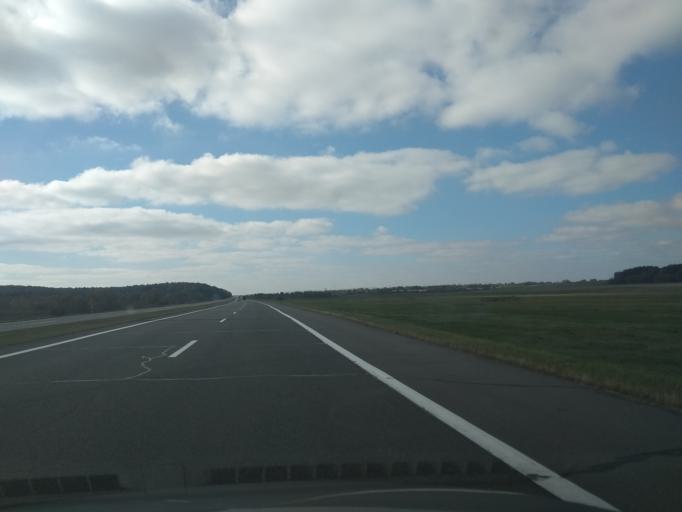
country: BY
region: Minsk
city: Snow
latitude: 53.2525
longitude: 26.2257
